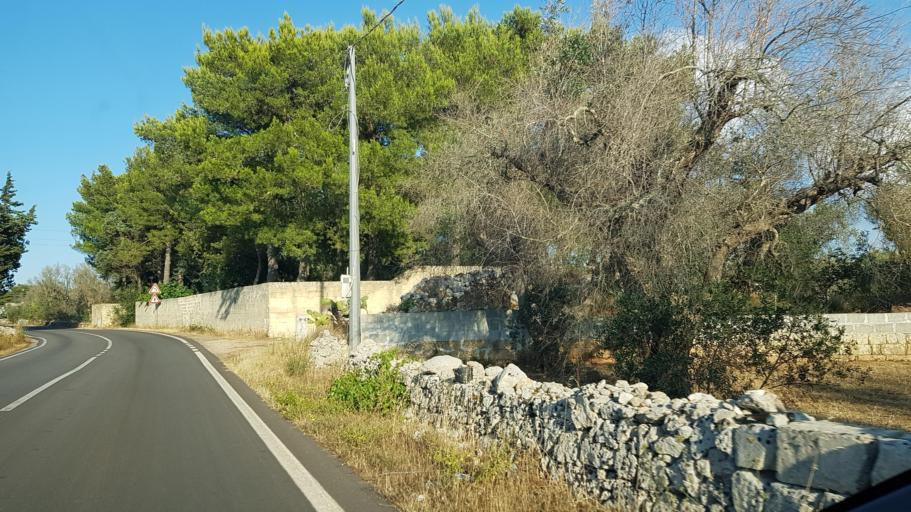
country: IT
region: Apulia
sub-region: Provincia di Lecce
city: Andrano
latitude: 39.9816
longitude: 18.3717
